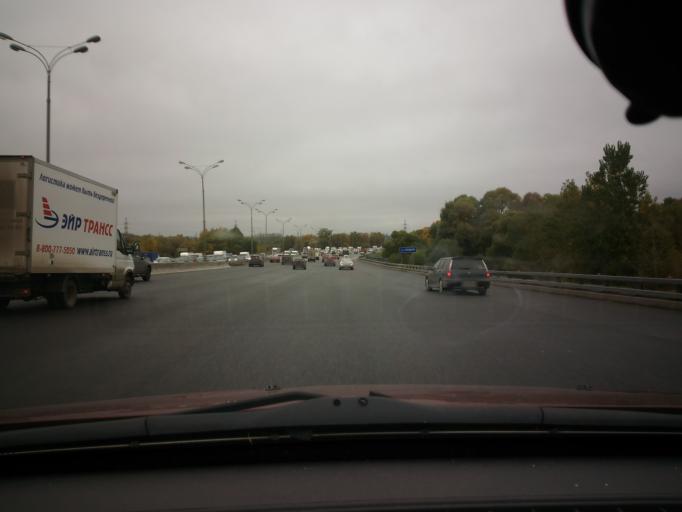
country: RU
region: Moscow
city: Strogino
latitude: 55.8423
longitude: 37.3941
